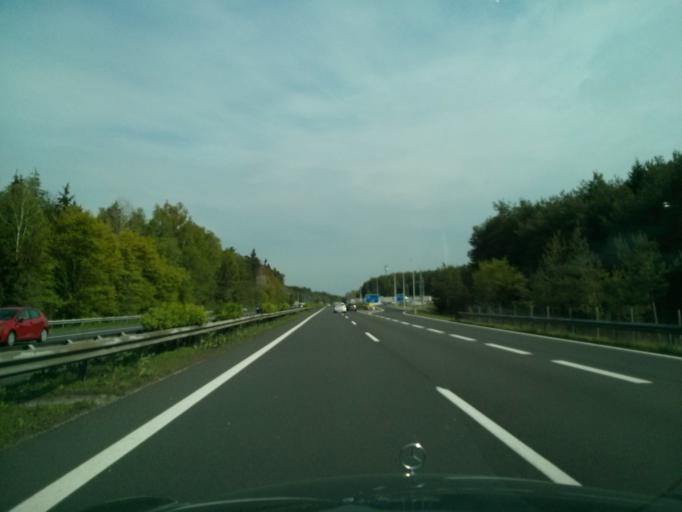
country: AT
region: Styria
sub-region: Politischer Bezirk Hartberg-Fuerstenfeld
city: Hainersdorf
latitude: 47.1133
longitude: 15.9847
